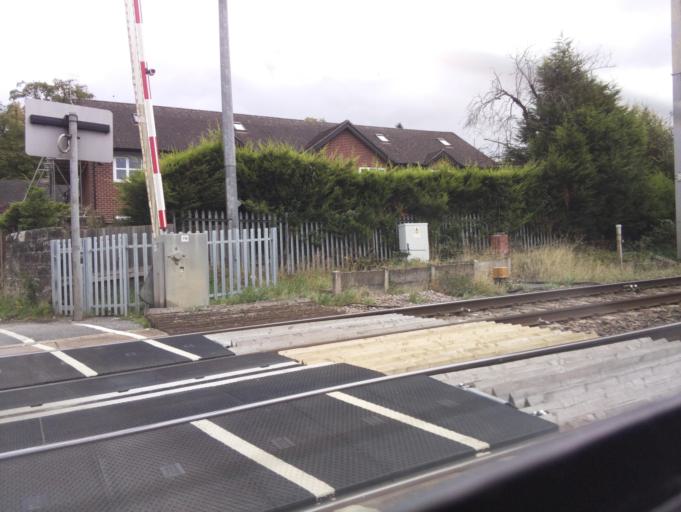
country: GB
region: England
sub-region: Staffordshire
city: Barlaston
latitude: 52.9423
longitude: -2.1680
